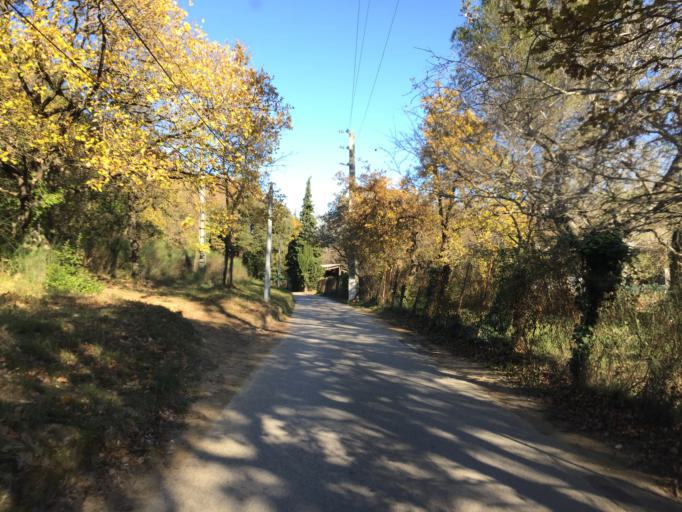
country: FR
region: Provence-Alpes-Cote d'Azur
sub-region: Departement du Vaucluse
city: Entraigues-sur-la-Sorgue
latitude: 44.0156
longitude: 4.9099
